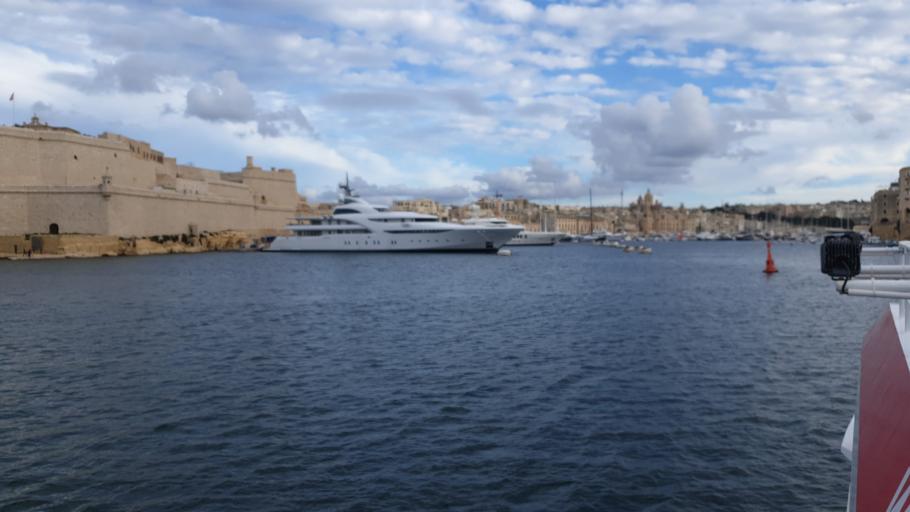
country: MT
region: Il-Birgu
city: Vittoriosa
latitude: 35.8922
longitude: 14.5148
